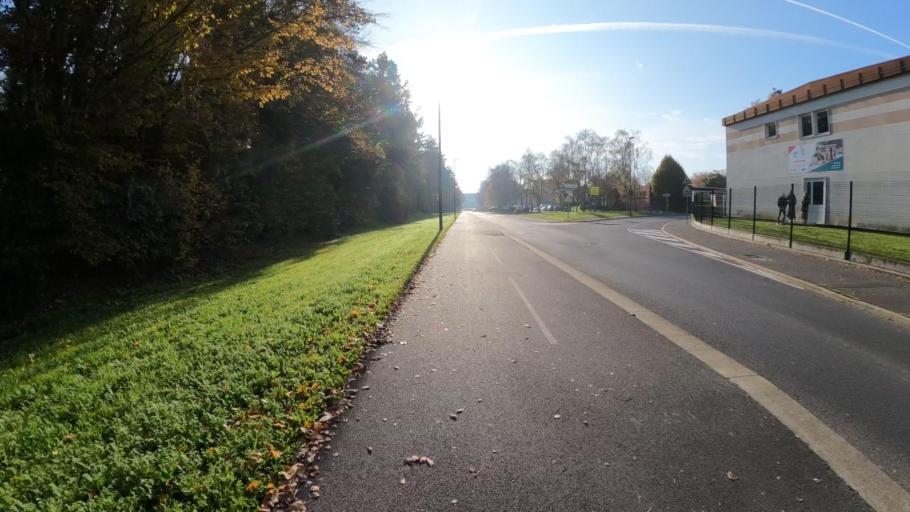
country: FR
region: Lower Normandy
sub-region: Departement du Calvados
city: Herouville-Saint-Clair
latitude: 49.2073
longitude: -0.3349
